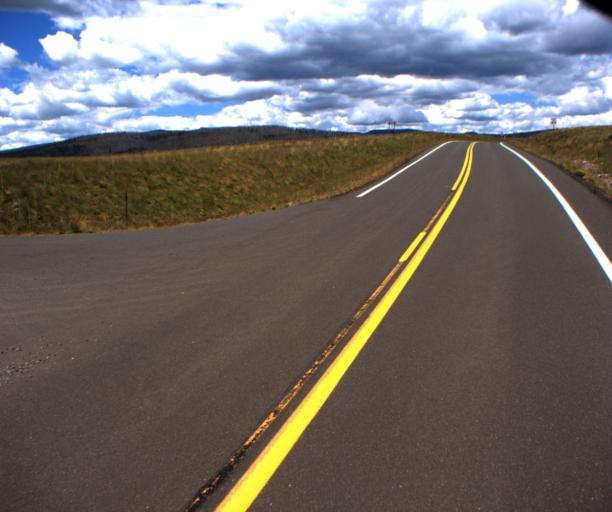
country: US
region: Arizona
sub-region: Apache County
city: Eagar
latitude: 33.9184
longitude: -109.4268
